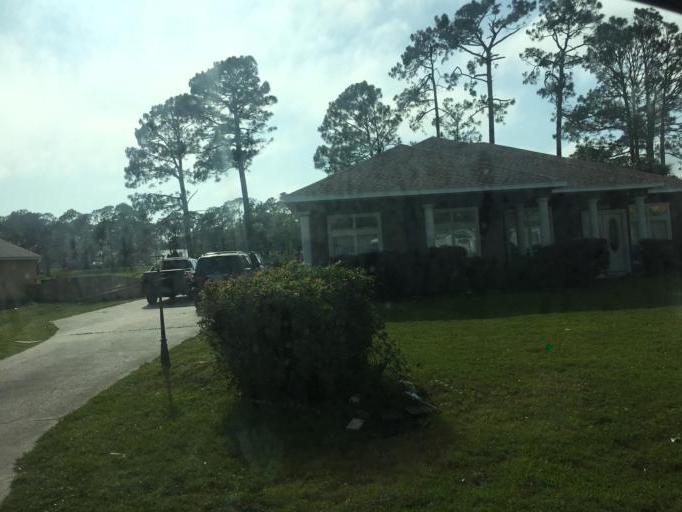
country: US
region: Florida
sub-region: Bay County
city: Panama City Beach
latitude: 30.2153
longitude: -85.8417
